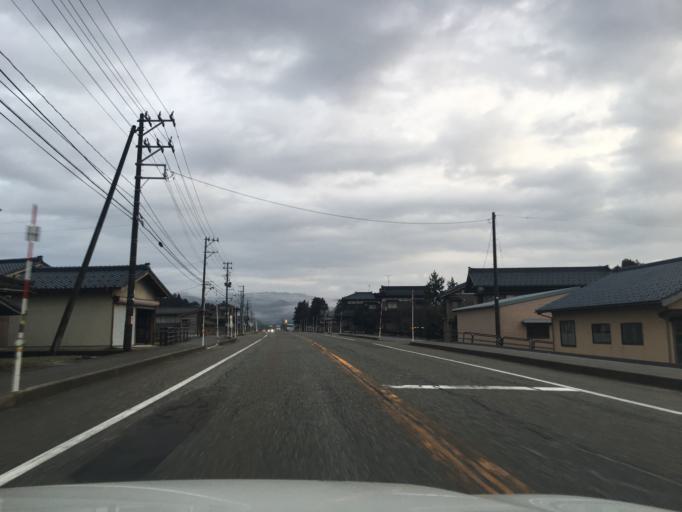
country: JP
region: Niigata
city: Murakami
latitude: 38.3137
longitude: 139.5485
